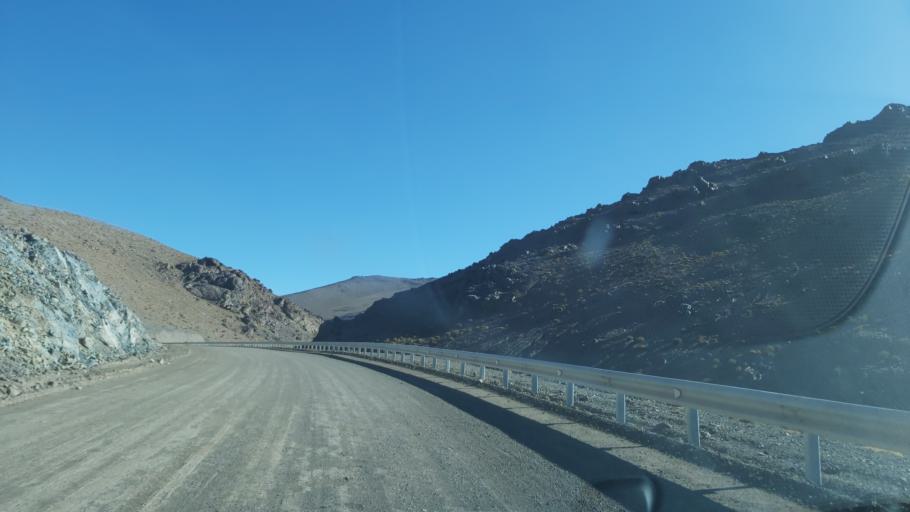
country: CL
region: Atacama
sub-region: Provincia de Chanaral
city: Diego de Almagro
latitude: -26.3978
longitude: -69.2809
